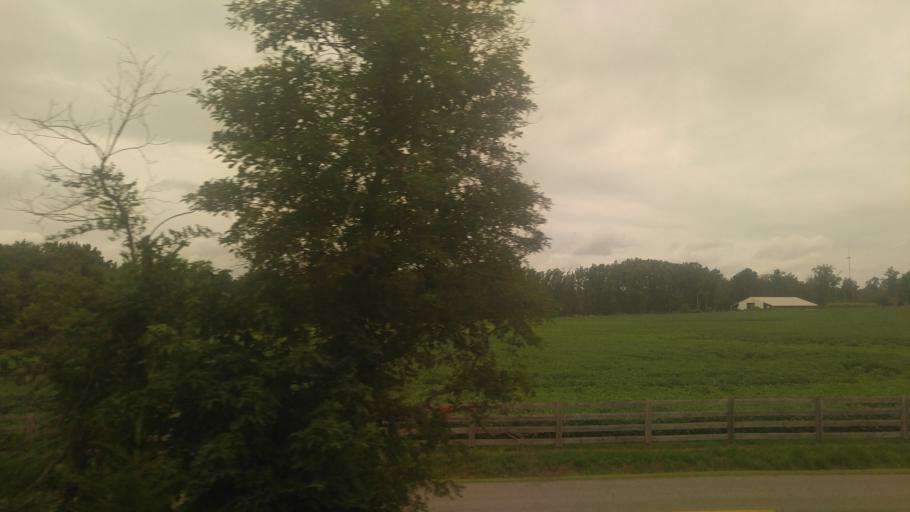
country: US
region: Virginia
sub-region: Hanover County
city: Ashland
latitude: 37.7398
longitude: -77.4872
